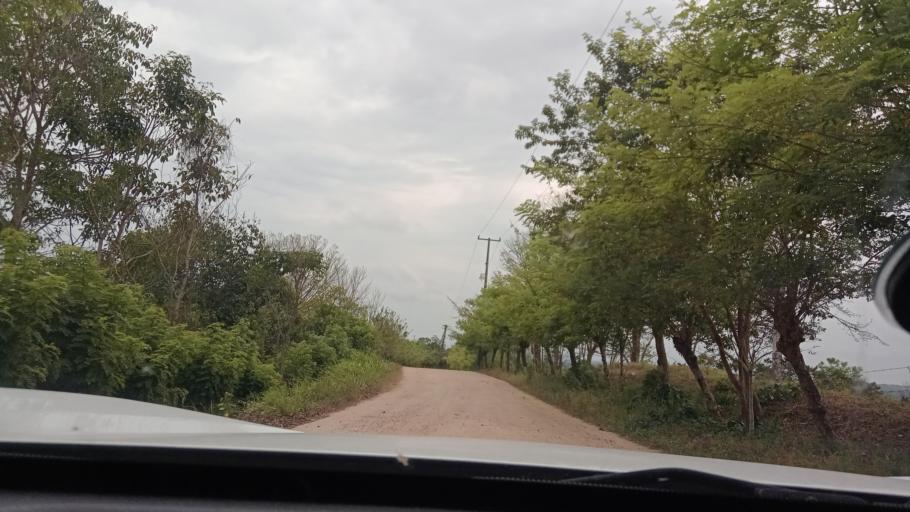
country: MX
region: Tabasco
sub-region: Huimanguillo
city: Francisco Rueda
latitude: 17.5804
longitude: -94.0685
